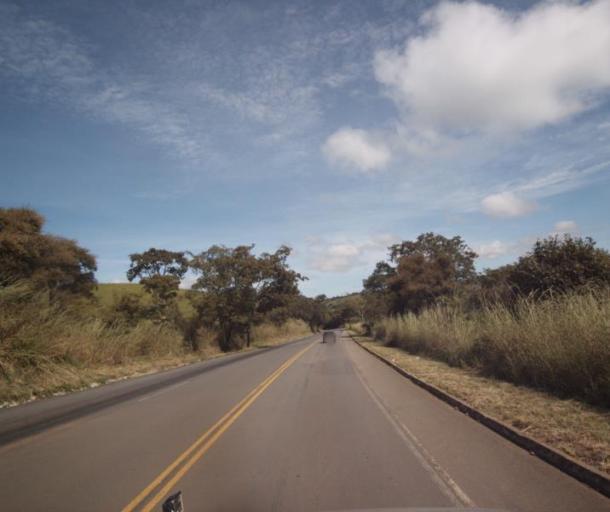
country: BR
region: Goias
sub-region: Abadiania
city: Abadiania
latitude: -16.1030
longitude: -48.8609
